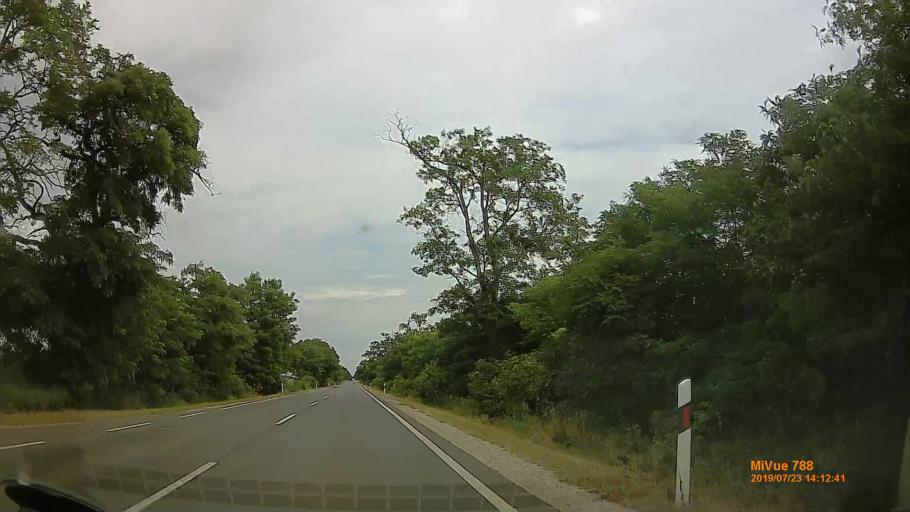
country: HU
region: Szabolcs-Szatmar-Bereg
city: Nagycserkesz
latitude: 47.9588
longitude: 21.4583
